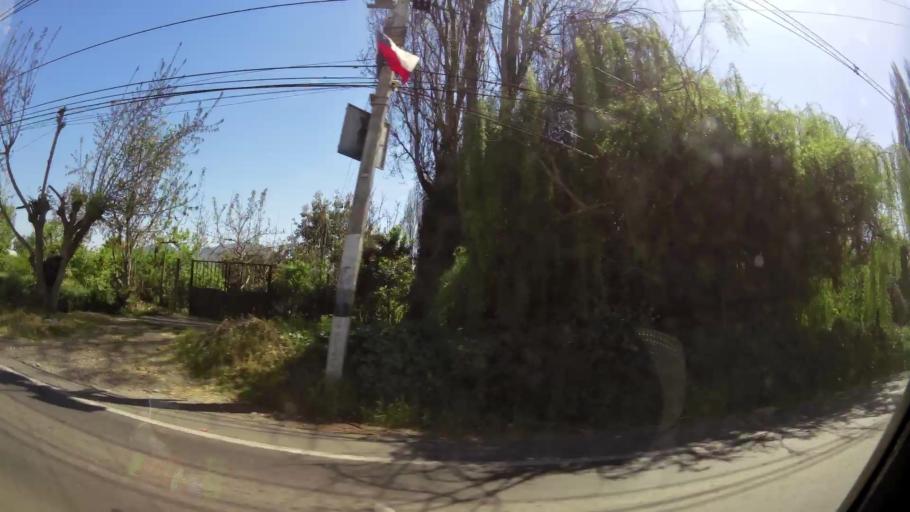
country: CL
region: Santiago Metropolitan
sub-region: Provincia de Talagante
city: Talagante
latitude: -33.6330
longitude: -70.9111
